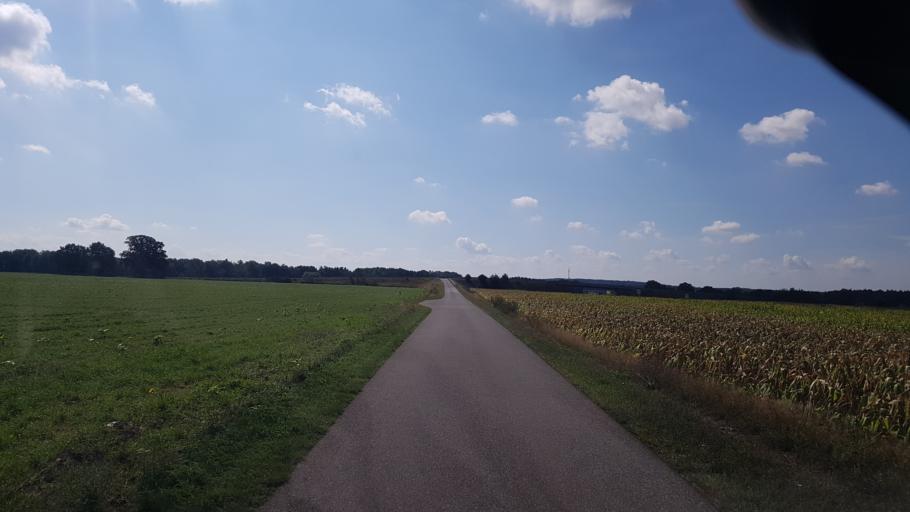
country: DE
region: Brandenburg
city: Drebkau
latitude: 51.6567
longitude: 14.2450
